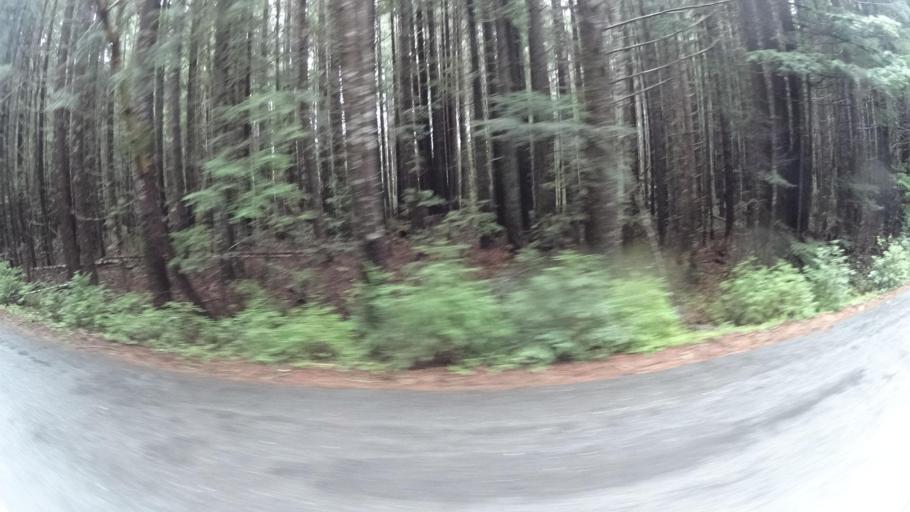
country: US
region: California
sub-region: Humboldt County
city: Westhaven-Moonstone
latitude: 41.2396
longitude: -123.9828
